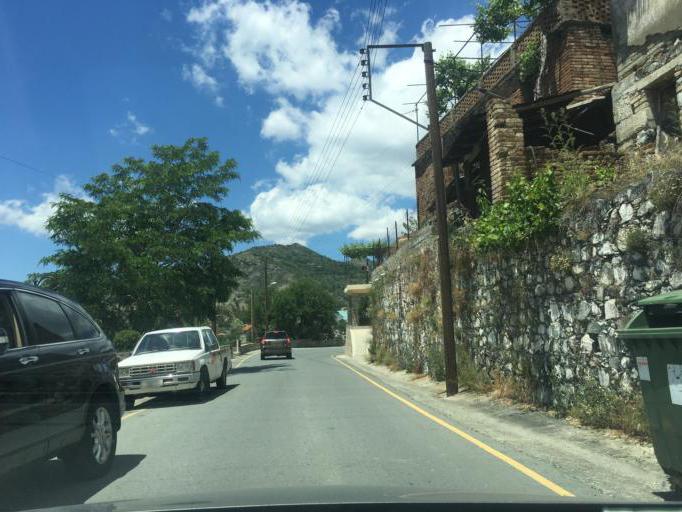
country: CY
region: Limassol
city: Kyperounta
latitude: 34.9136
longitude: 33.0236
